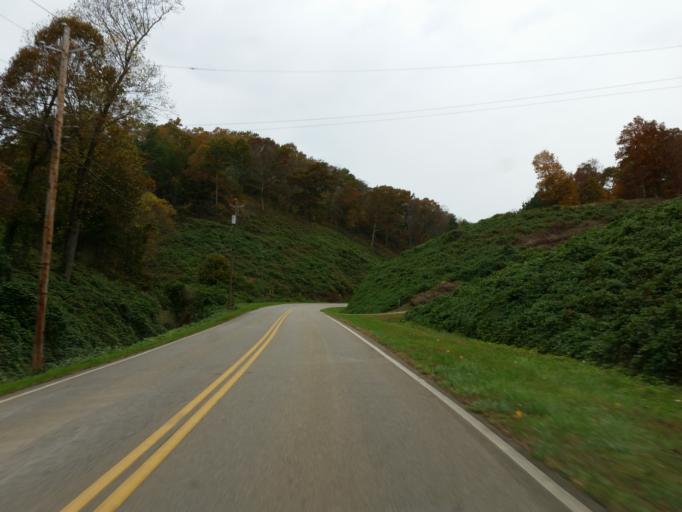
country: US
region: Georgia
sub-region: Pickens County
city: Jasper
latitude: 34.4967
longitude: -84.4314
